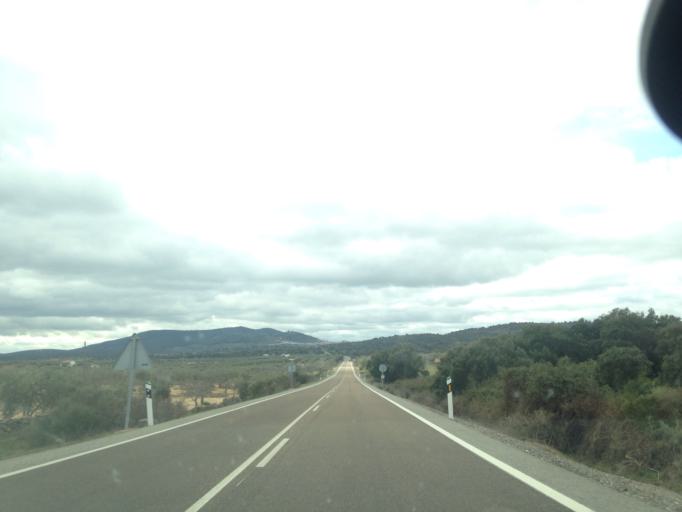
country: ES
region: Extremadura
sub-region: Provincia de Caceres
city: Montanchez
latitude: 39.2099
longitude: -6.1818
